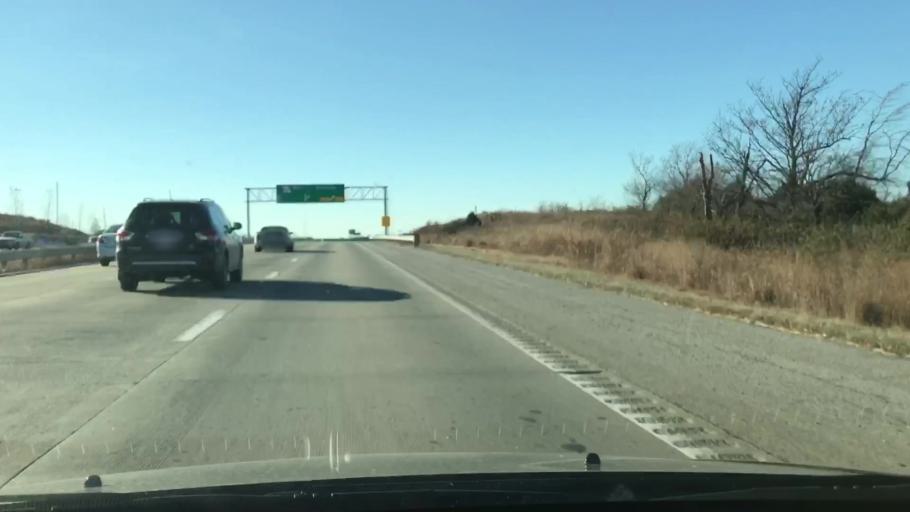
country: US
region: Missouri
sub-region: Jackson County
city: Grandview
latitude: 38.8585
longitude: -94.5406
